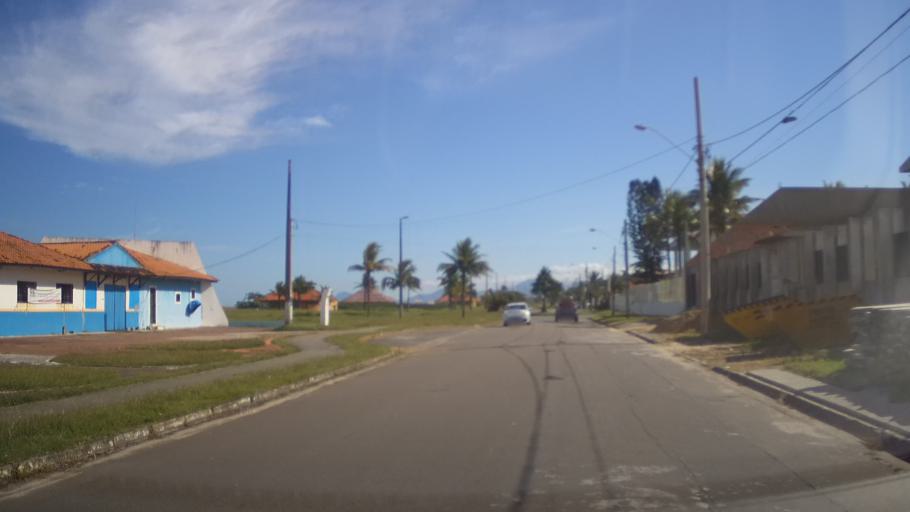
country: BR
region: Sao Paulo
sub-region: Itanhaem
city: Itanhaem
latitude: -24.2061
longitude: -46.8270
